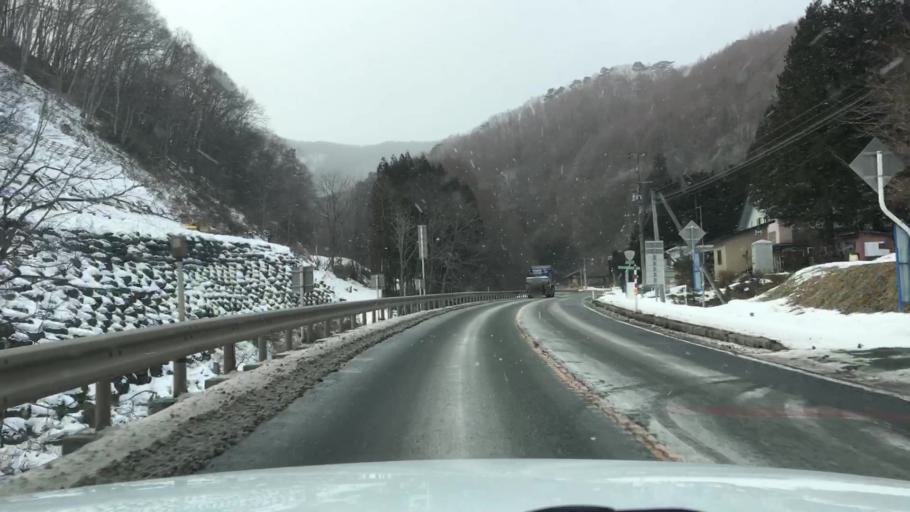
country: JP
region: Iwate
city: Tono
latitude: 39.6141
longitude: 141.4825
